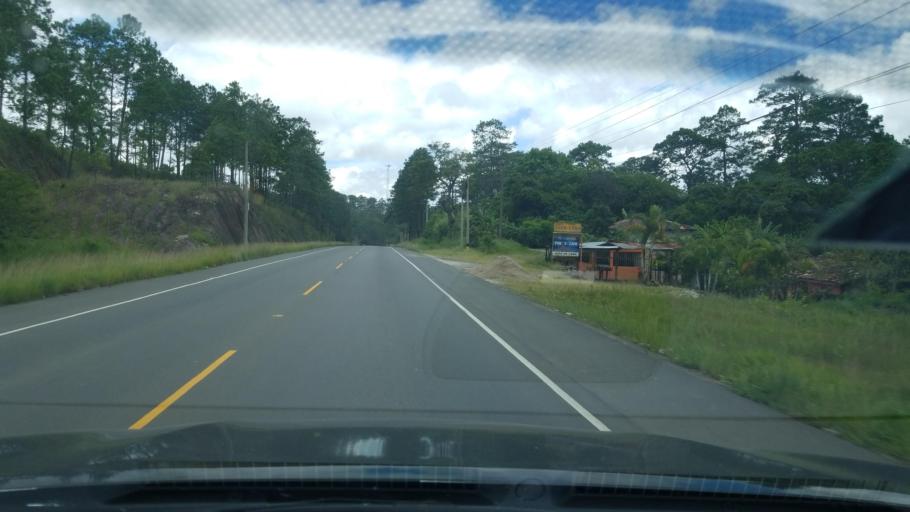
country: HN
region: Francisco Morazan
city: Talanga
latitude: 14.3559
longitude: -87.1523
